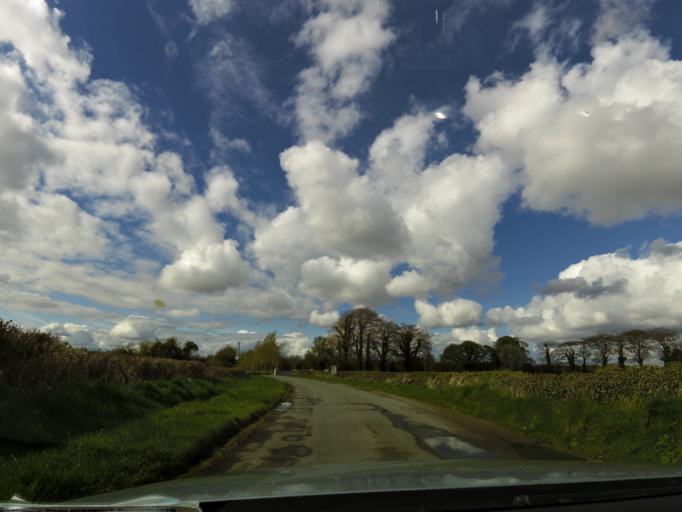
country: IE
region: Leinster
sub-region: Laois
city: Rathdowney
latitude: 52.7811
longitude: -7.5457
